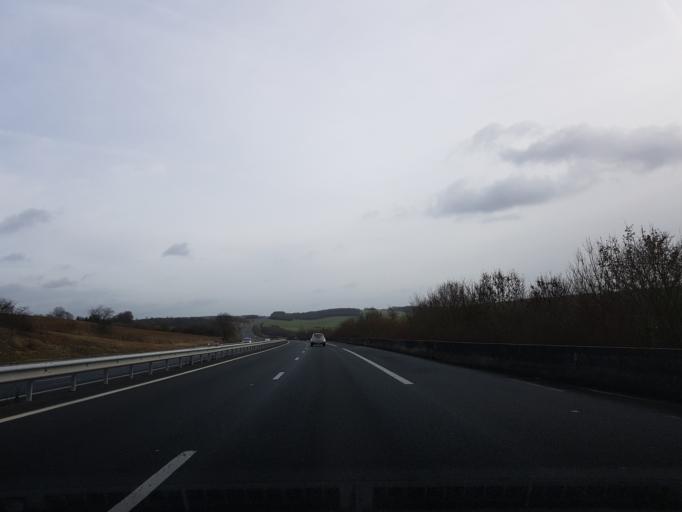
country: FR
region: Bourgogne
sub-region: Departement de l'Yonne
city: Thorigny-sur-Oreuse
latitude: 48.2349
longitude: 3.3874
